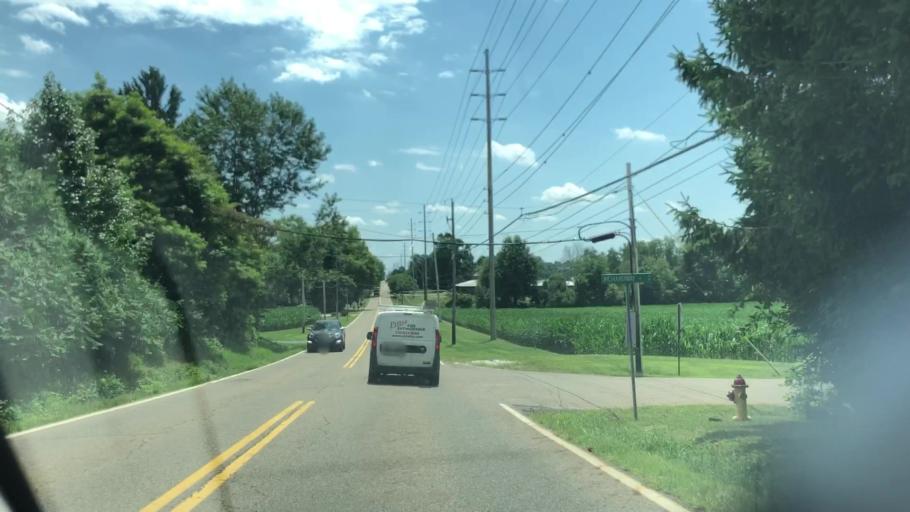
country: US
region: Ohio
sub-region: Summit County
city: Greensburg
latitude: 40.9034
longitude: -81.4980
